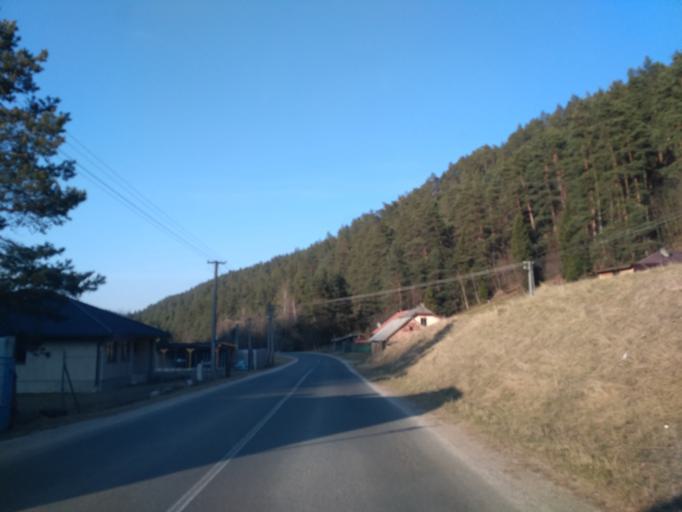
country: SK
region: Kosicky
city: Medzev
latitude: 48.7486
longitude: 20.7766
